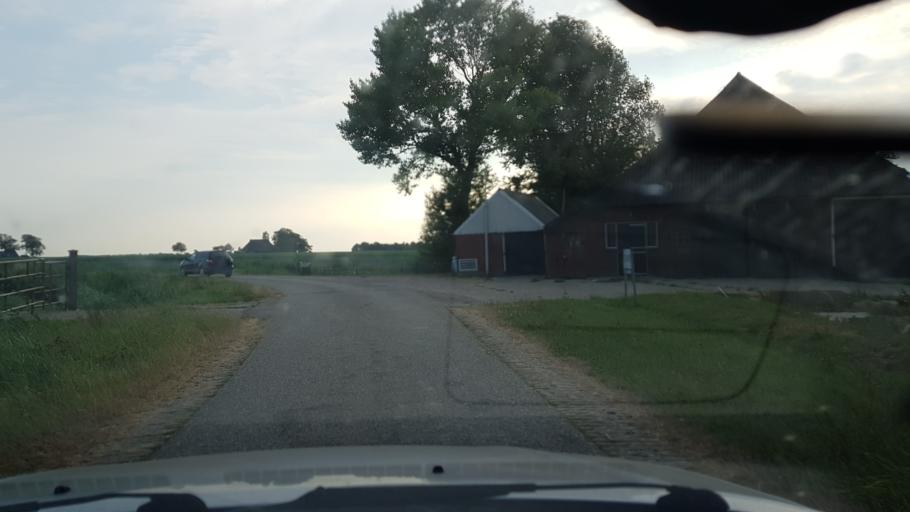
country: NL
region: Friesland
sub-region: Gemeente Ferwerderadiel
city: Burdaard
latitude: 53.3359
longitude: 5.8689
